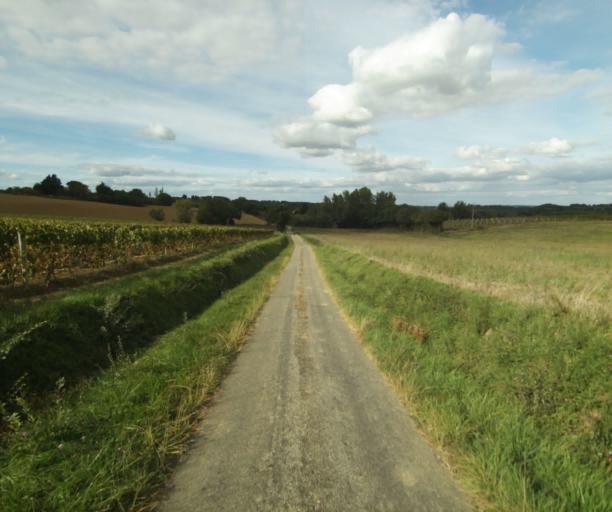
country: FR
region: Midi-Pyrenees
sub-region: Departement du Gers
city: Gondrin
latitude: 43.8562
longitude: 0.2722
